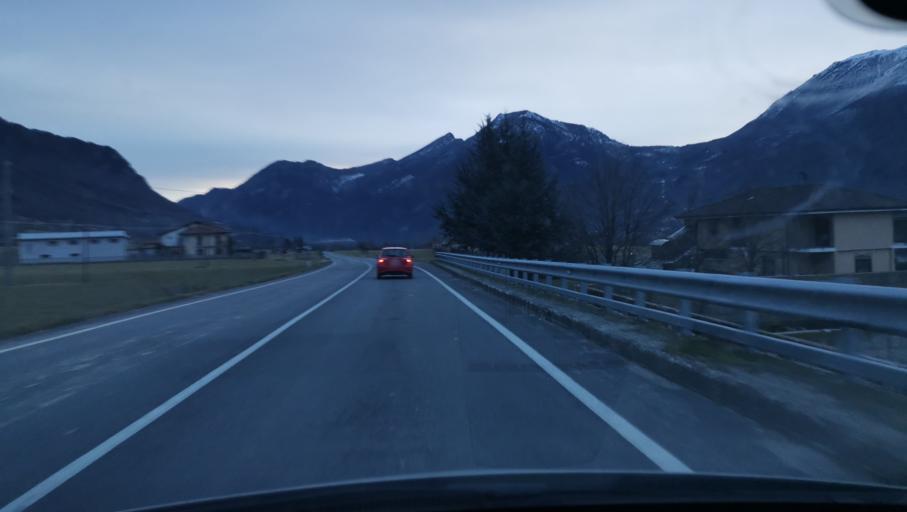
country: IT
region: Piedmont
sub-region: Provincia di Cuneo
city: Demonte
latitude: 44.3155
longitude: 7.3208
